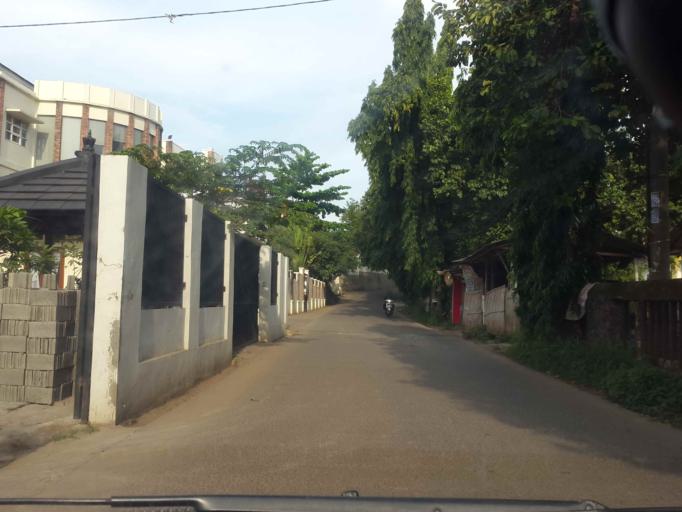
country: ID
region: Banten
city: South Tangerang
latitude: -6.2813
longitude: 106.6954
